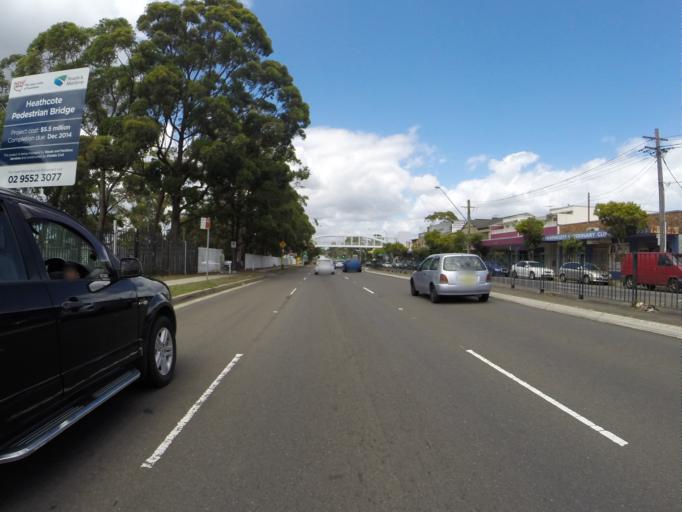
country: AU
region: New South Wales
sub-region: Sutherland Shire
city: Heathcote
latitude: -34.0868
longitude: 151.0089
